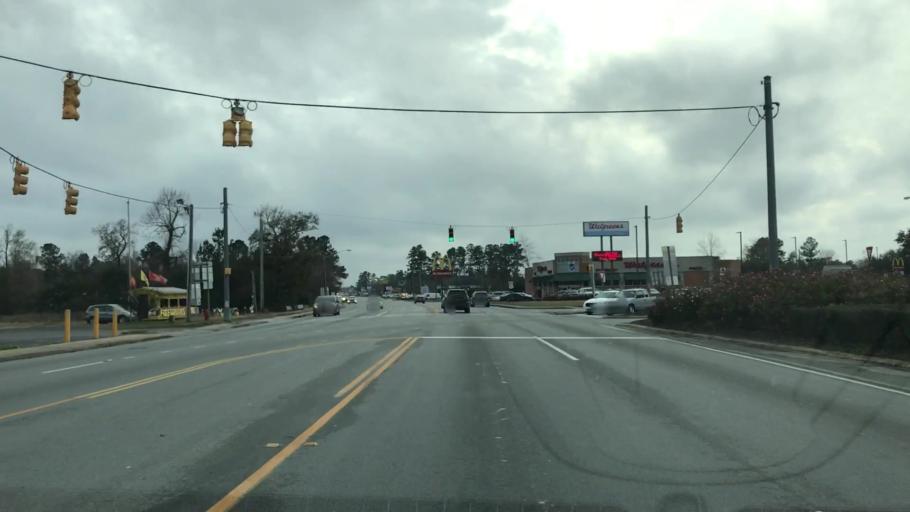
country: US
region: South Carolina
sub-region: Berkeley County
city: Moncks Corner
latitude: 33.2025
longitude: -79.9895
